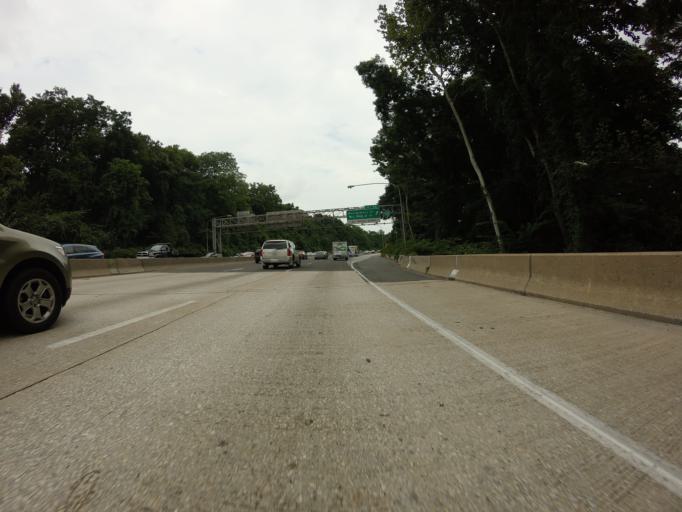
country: US
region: Pennsylvania
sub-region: Montgomery County
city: Bala-Cynwyd
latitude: 39.9823
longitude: -75.2075
